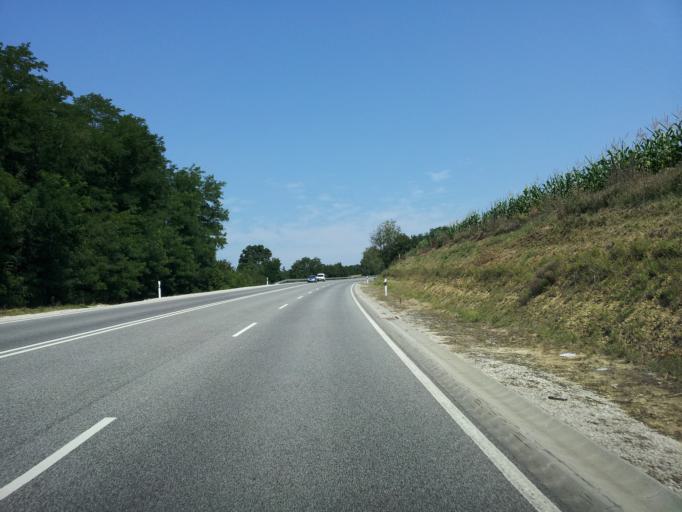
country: HU
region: Zala
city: Pacsa
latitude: 46.8166
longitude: 17.0551
